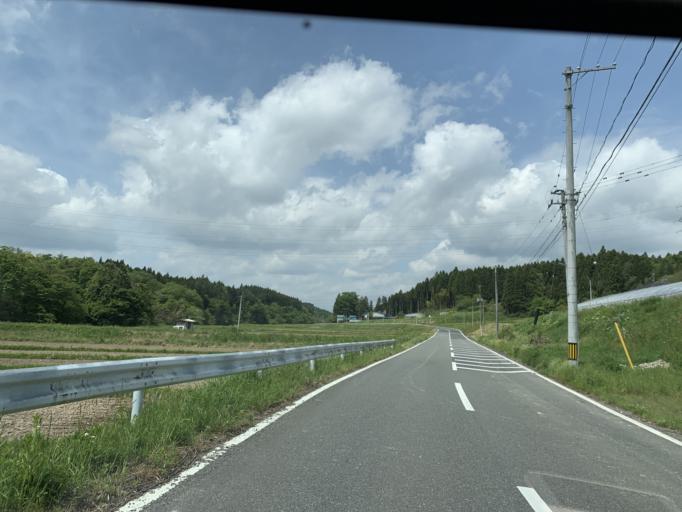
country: JP
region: Miyagi
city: Furukawa
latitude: 38.7722
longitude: 140.9796
